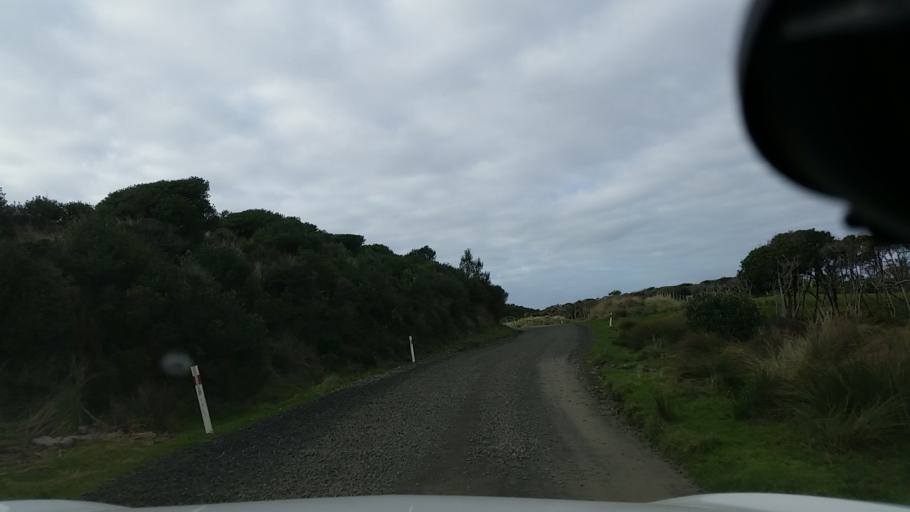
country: NZ
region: Chatham Islands
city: Waitangi
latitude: -43.7490
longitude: -176.4182
